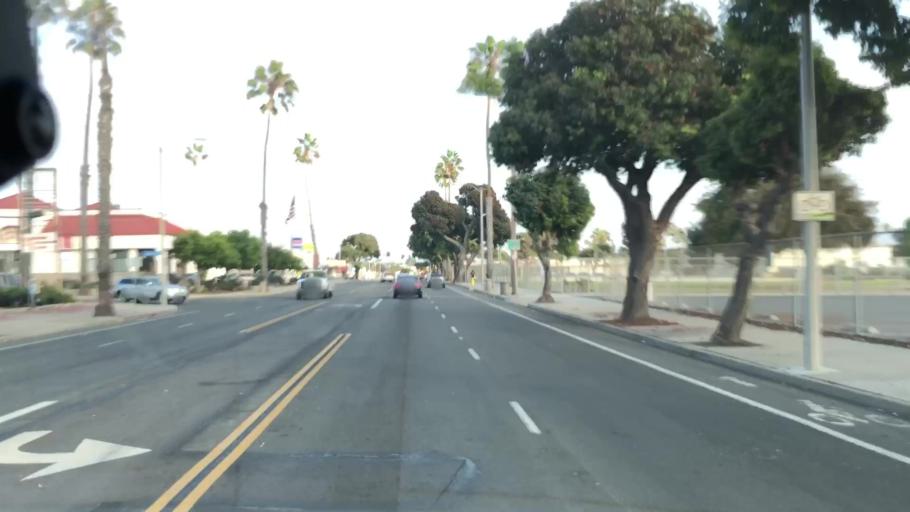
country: US
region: California
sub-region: Ventura County
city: Ventura
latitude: 34.2729
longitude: -119.2628
